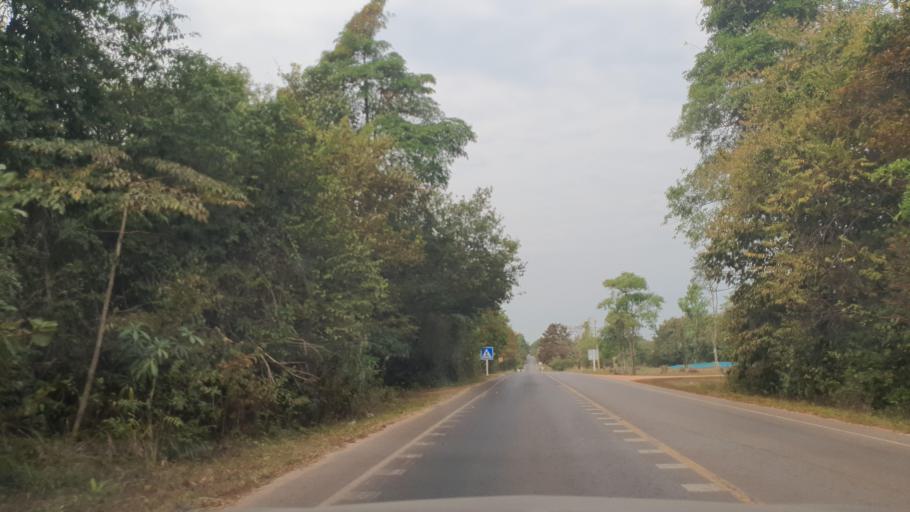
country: TH
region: Changwat Bueng Kan
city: Bung Khla
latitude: 18.2386
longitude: 104.0241
